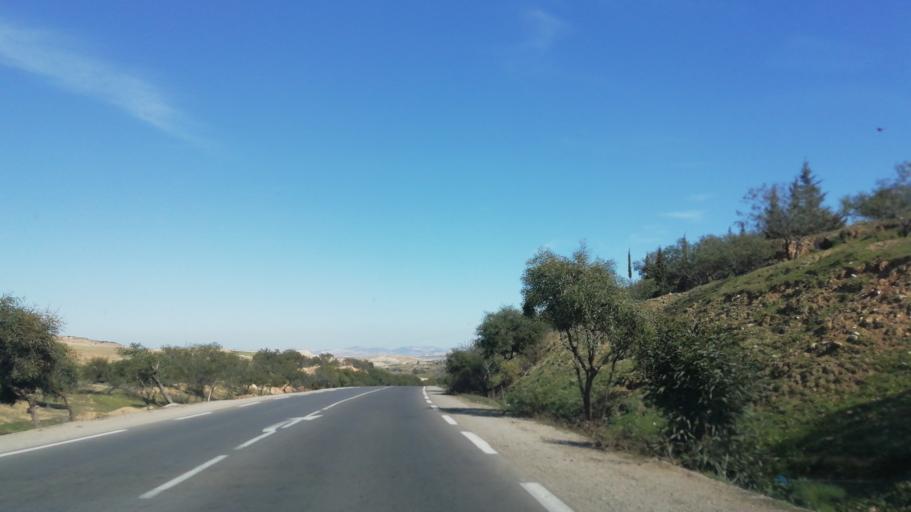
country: DZ
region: Mascara
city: Oued el Abtal
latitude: 35.4370
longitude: 0.4982
